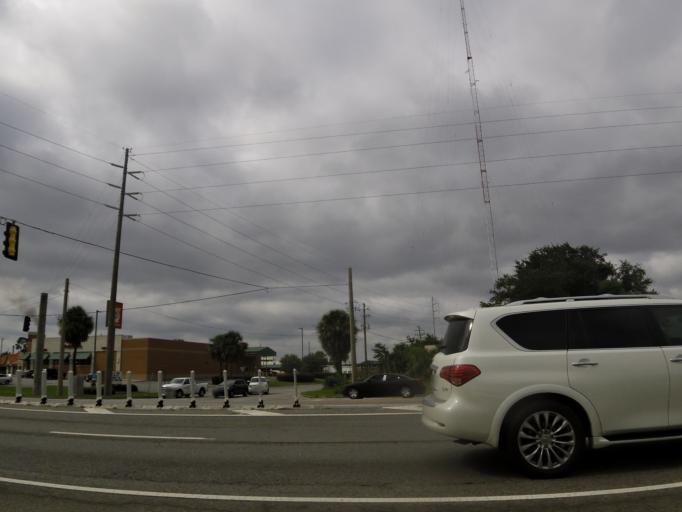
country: US
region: Georgia
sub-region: Glynn County
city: Brunswick
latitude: 31.1612
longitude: -81.4744
